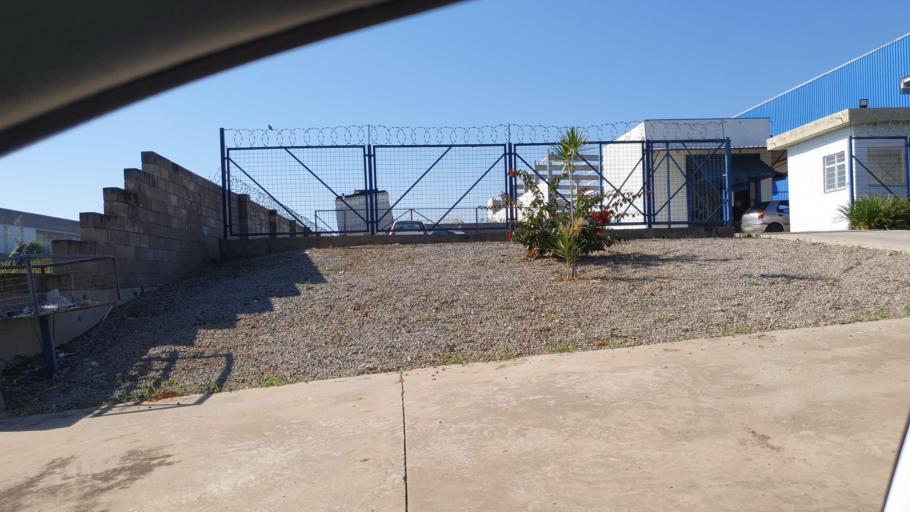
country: BR
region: Sao Paulo
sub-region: Sorocaba
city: Sorocaba
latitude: -23.4431
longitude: -47.4404
